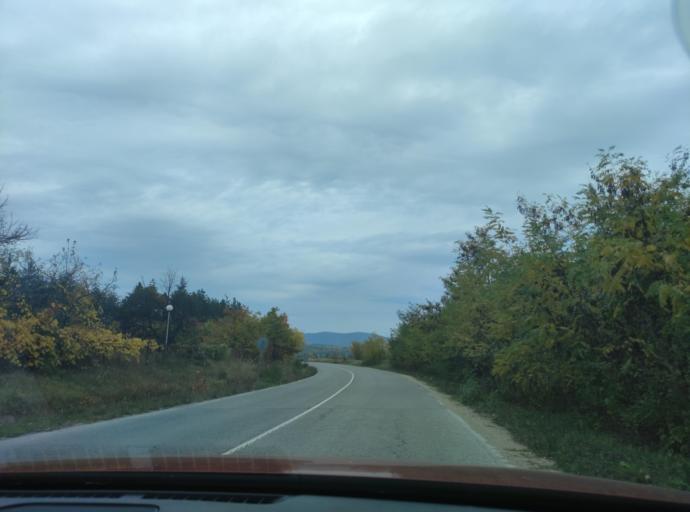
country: BG
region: Montana
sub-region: Obshtina Berkovitsa
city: Berkovitsa
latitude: 43.2207
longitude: 23.1593
